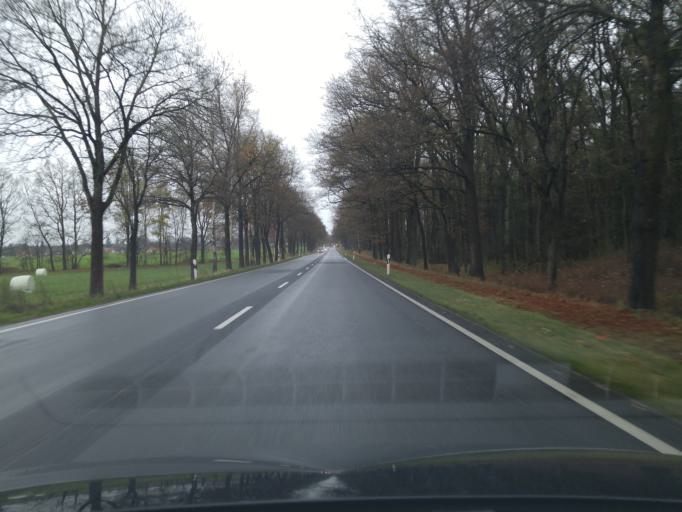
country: DE
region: Lower Saxony
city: Sprakensehl
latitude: 52.7557
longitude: 10.4918
